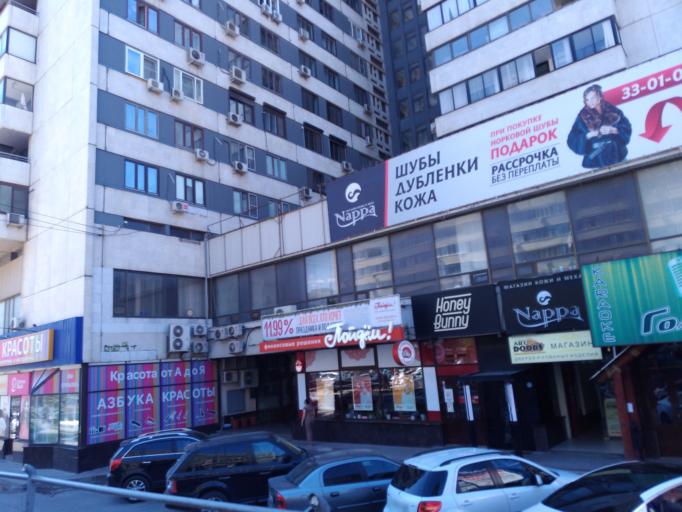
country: RU
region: Volgograd
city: Volgograd
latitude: 48.7042
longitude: 44.5103
